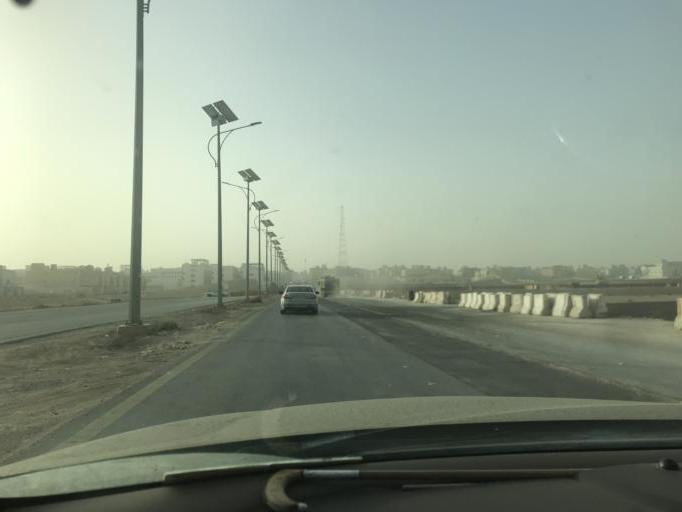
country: SA
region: Ar Riyad
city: Riyadh
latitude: 24.8465
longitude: 46.6638
